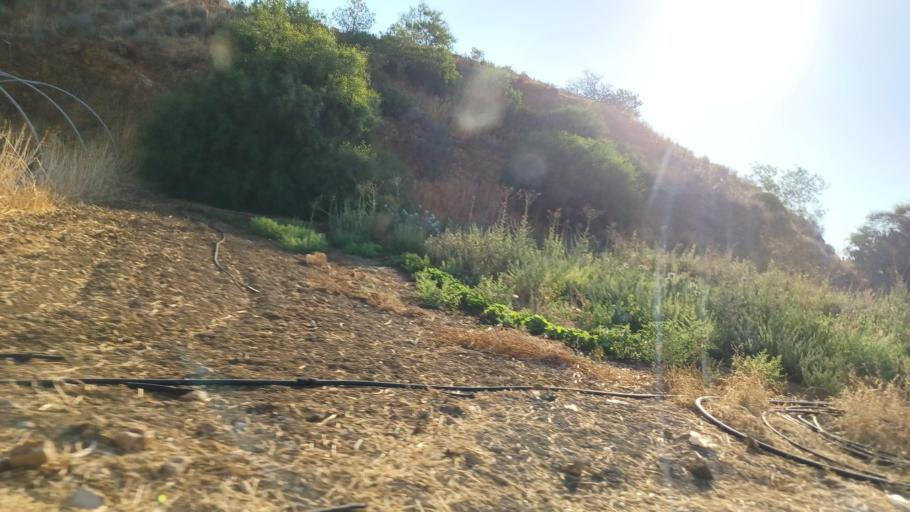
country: CY
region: Larnaka
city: Troulloi
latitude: 35.0080
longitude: 33.6113
